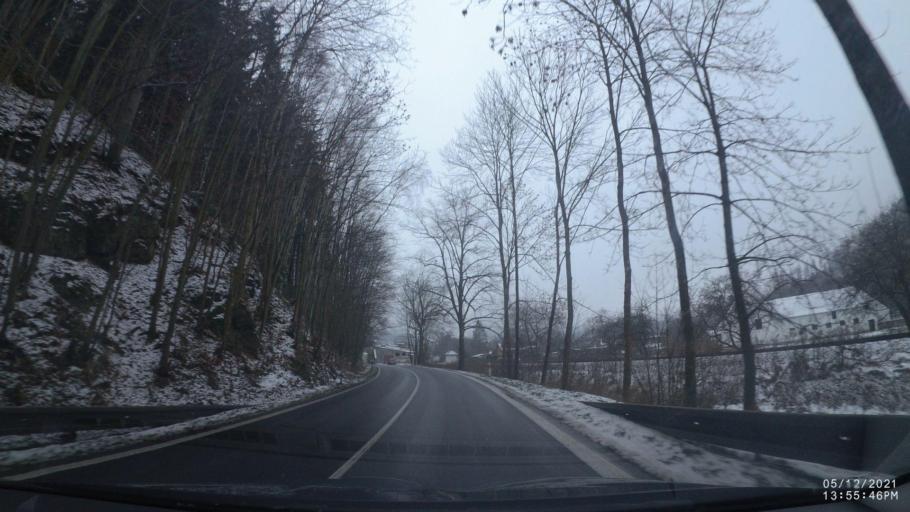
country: CZ
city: Hronov
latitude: 50.4965
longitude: 16.1971
